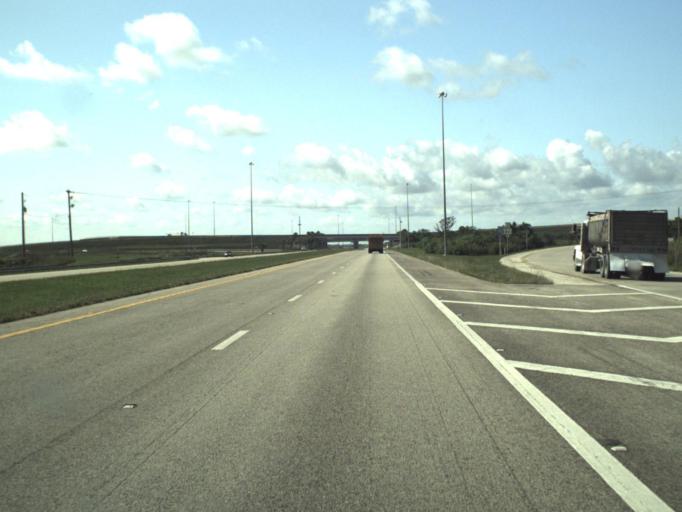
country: US
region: Florida
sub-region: Broward County
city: Weston
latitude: 26.1511
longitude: -80.4435
